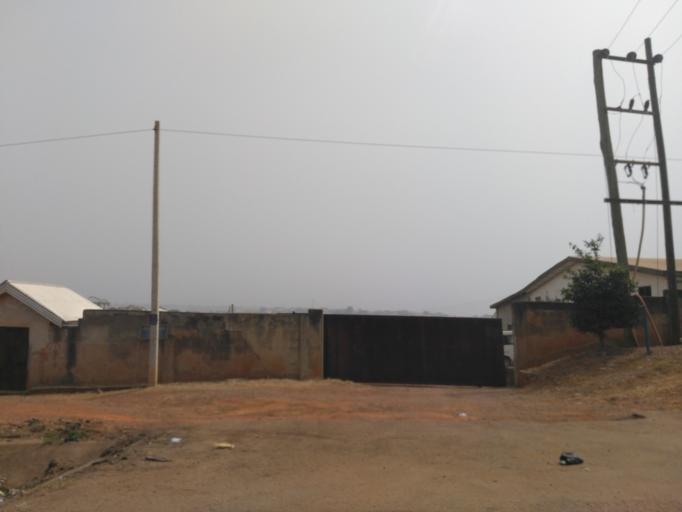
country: GH
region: Ashanti
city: Kumasi
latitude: 6.6434
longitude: -1.6448
